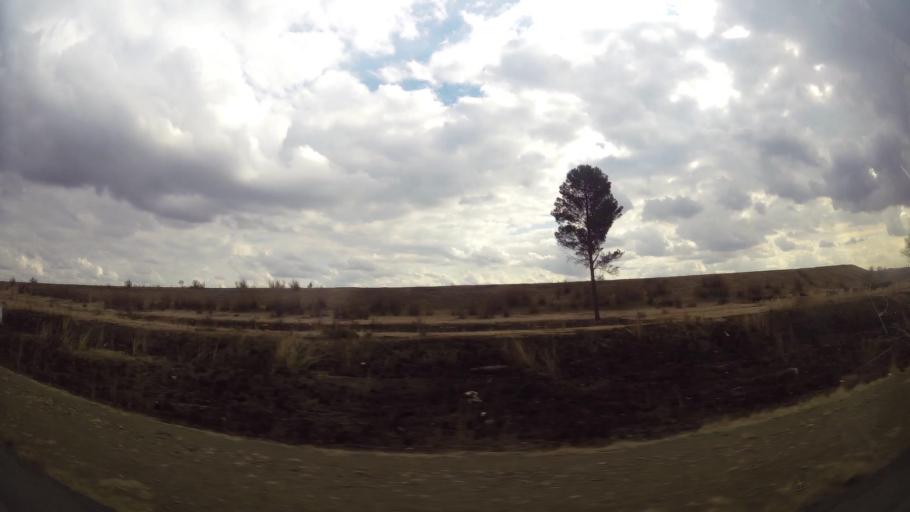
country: ZA
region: Orange Free State
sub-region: Fezile Dabi District Municipality
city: Sasolburg
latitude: -26.8723
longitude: 27.8872
